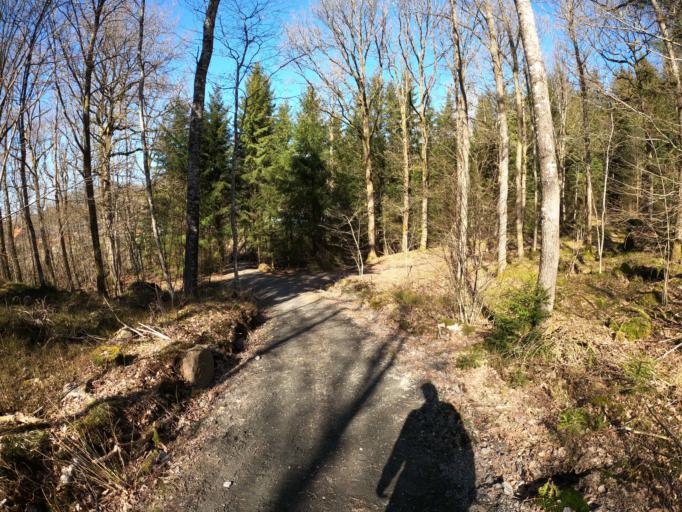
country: SE
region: Vaestra Goetaland
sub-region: Harryda Kommun
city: Molnlycke
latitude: 57.6258
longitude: 12.1115
